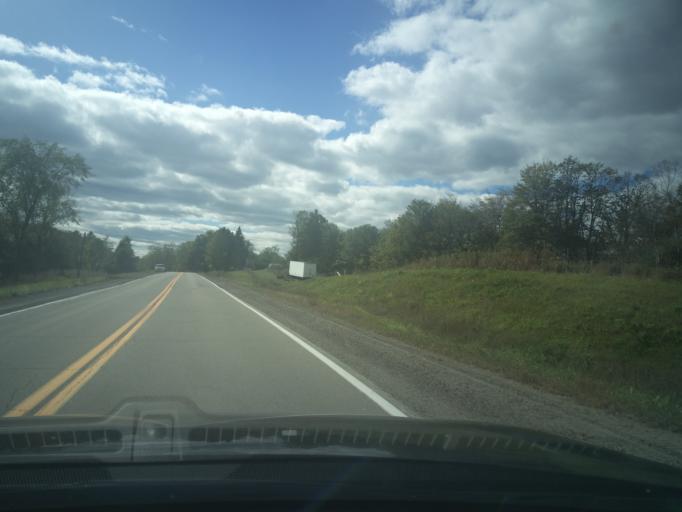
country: CA
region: Ontario
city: Perth
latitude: 44.7630
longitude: -76.3764
